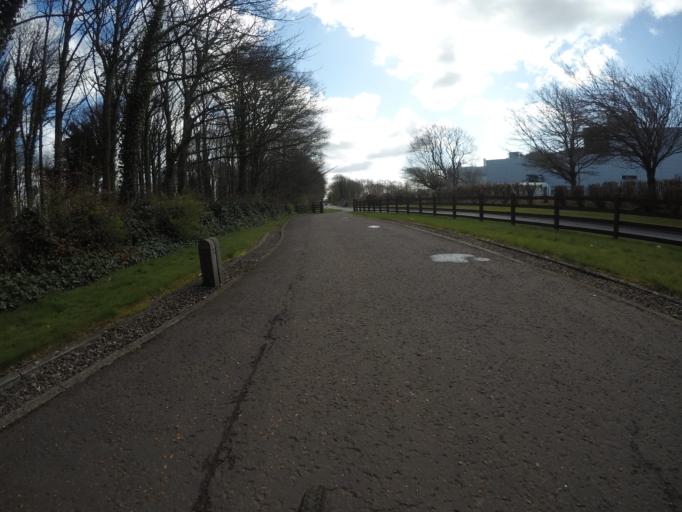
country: GB
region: Scotland
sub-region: North Ayrshire
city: Dreghorn
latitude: 55.5965
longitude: -4.6262
